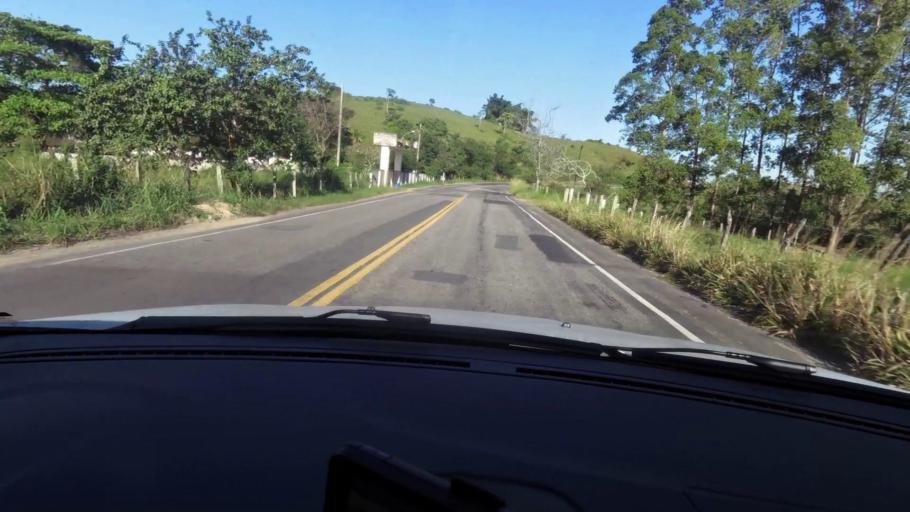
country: BR
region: Espirito Santo
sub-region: Piuma
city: Piuma
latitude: -20.7265
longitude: -40.6548
